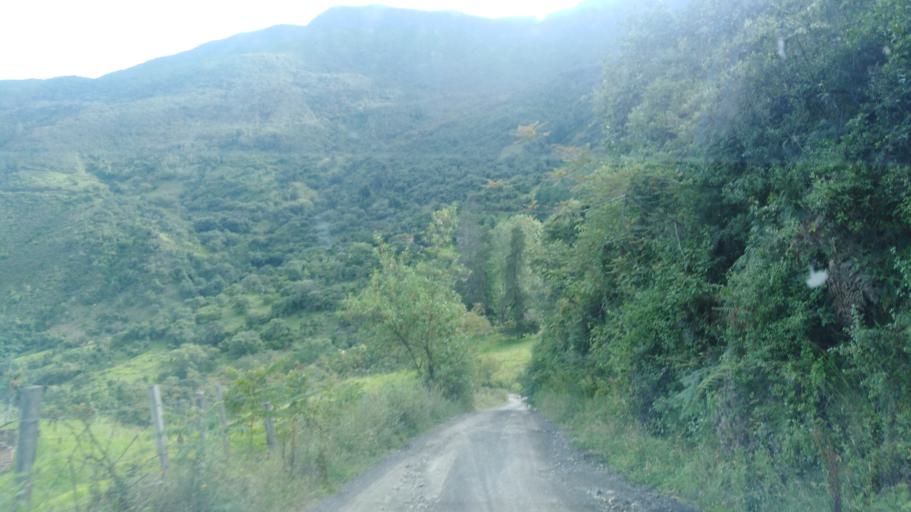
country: CO
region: Boyaca
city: San Mateo
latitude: 6.4214
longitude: -72.5622
